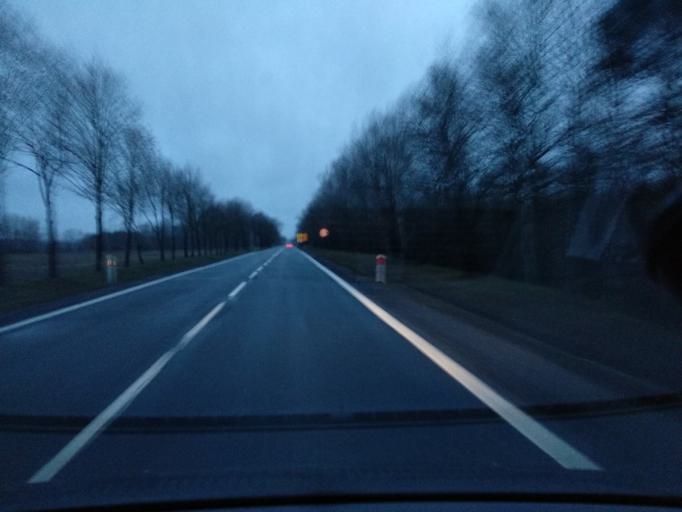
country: PL
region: Lower Silesian Voivodeship
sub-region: Powiat sredzki
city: Malczyce
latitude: 51.2219
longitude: 16.4438
